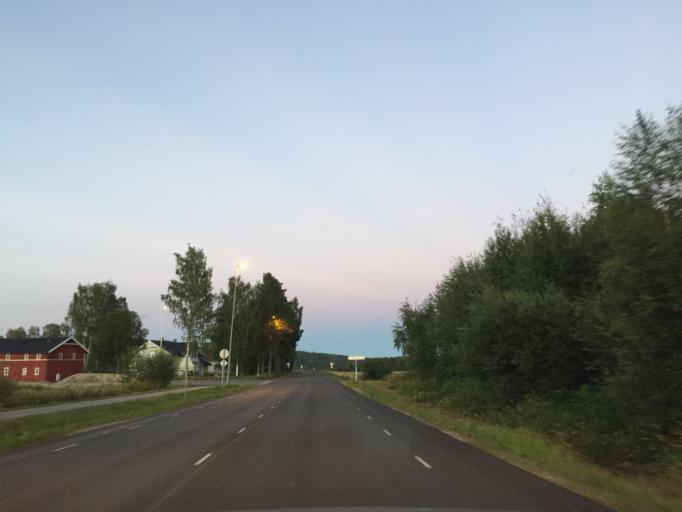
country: NO
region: Hedmark
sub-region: Kongsvinger
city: Spetalen
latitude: 60.2319
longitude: 11.8181
